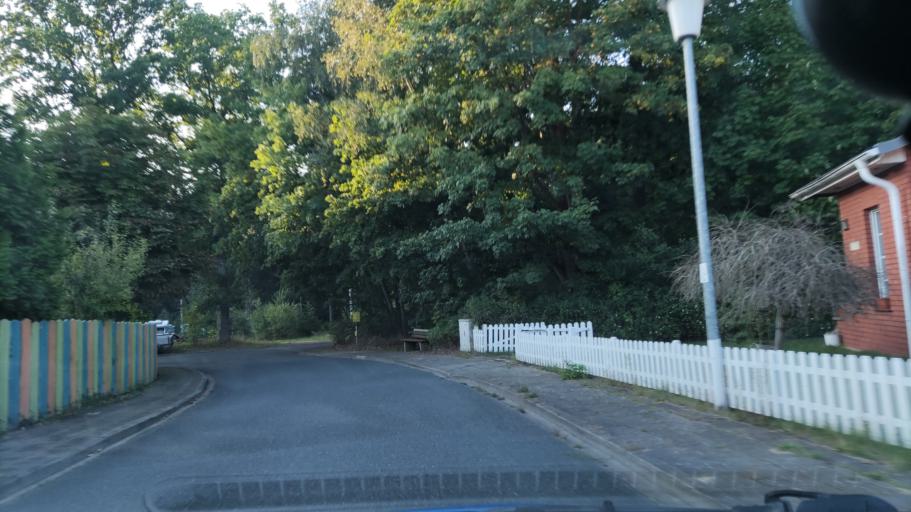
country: DE
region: Lower Saxony
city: Fassberg
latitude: 52.9631
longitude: 10.1862
